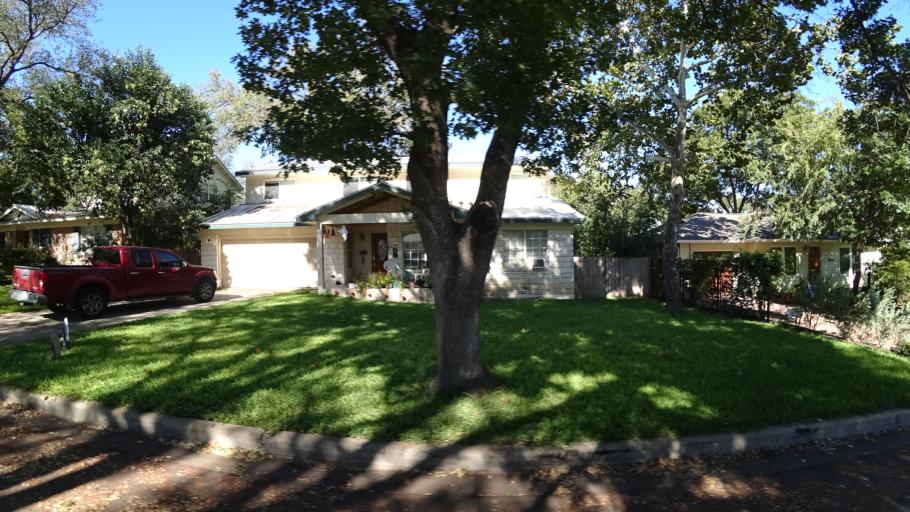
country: US
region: Texas
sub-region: Travis County
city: Austin
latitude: 30.3231
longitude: -97.7497
